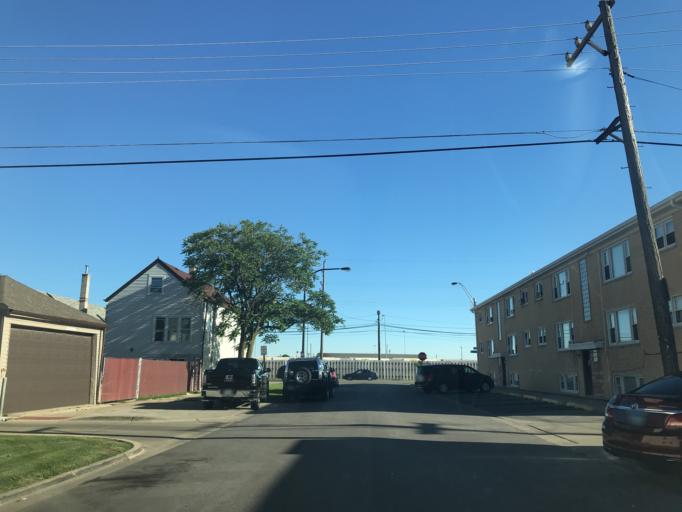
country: US
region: Illinois
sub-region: Cook County
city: Cicero
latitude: 41.8444
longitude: -87.7613
